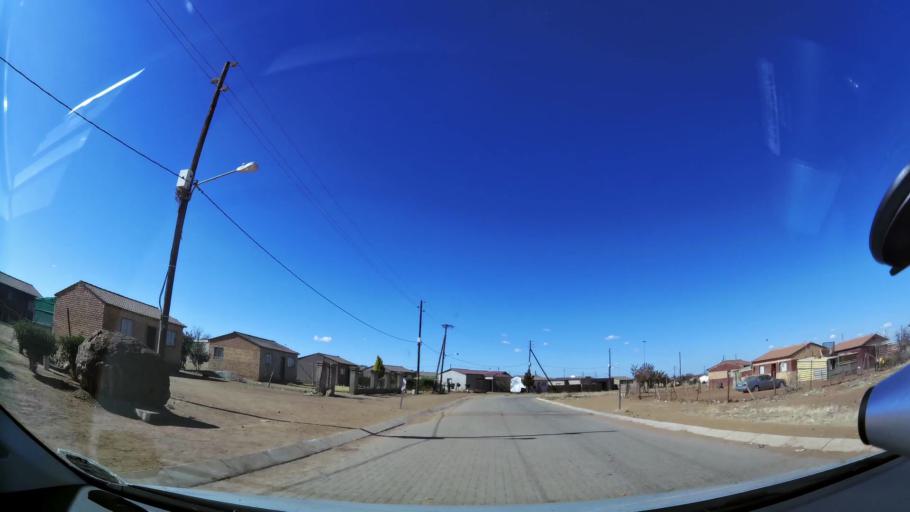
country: ZA
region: North-West
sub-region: Dr Kenneth Kaunda District Municipality
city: Klerksdorp
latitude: -26.8686
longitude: 26.5685
